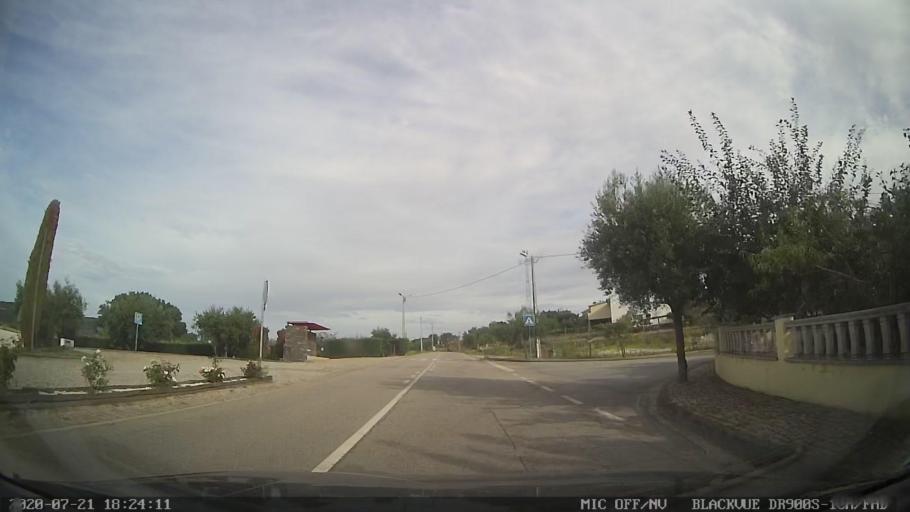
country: PT
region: Guarda
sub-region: Vila Nova de Foz Coa
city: Custoias
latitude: 41.0714
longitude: -7.3905
